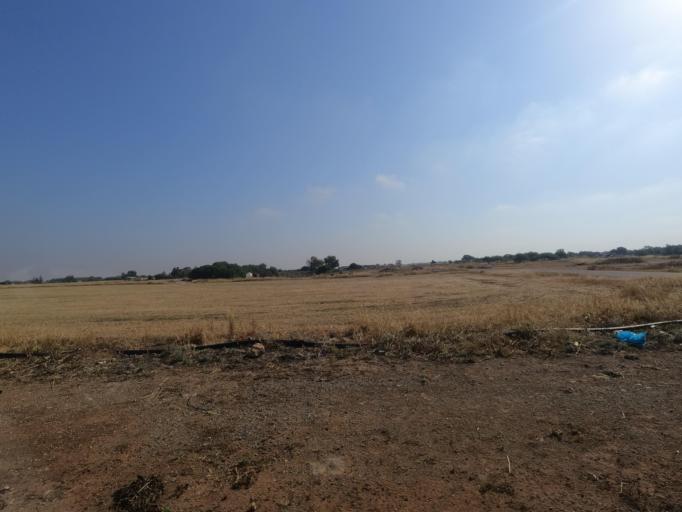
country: CY
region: Ammochostos
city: Avgorou
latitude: 35.0456
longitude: 33.8295
